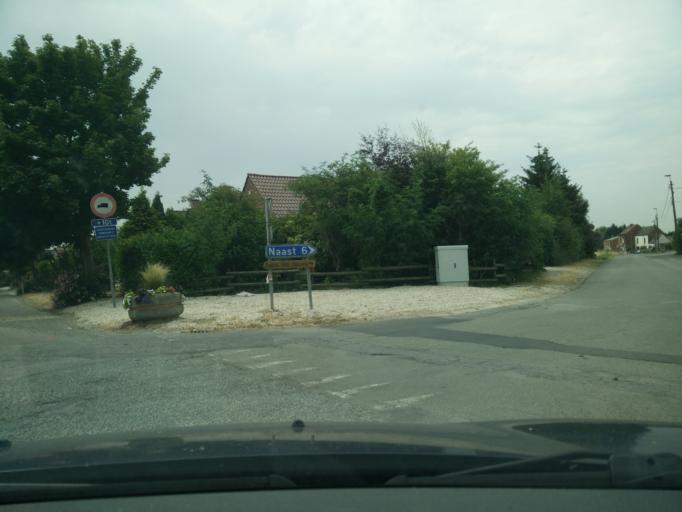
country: BE
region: Wallonia
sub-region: Province du Hainaut
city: Braine-le-Comte
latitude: 50.5907
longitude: 4.1329
